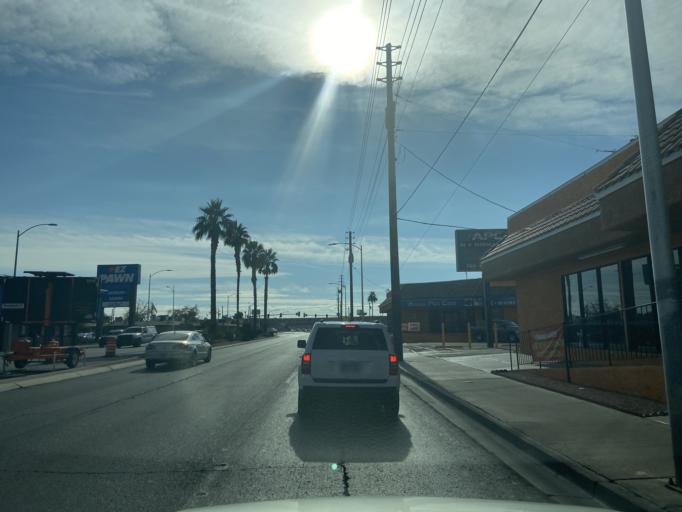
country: US
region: Nevada
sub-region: Clark County
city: Las Vegas
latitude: 36.1719
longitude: -115.1162
